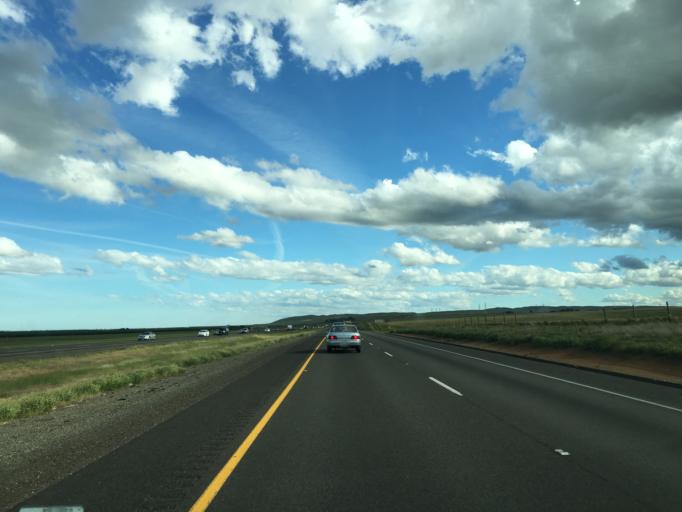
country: US
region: California
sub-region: Merced County
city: Los Banos
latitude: 36.9884
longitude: -120.9052
